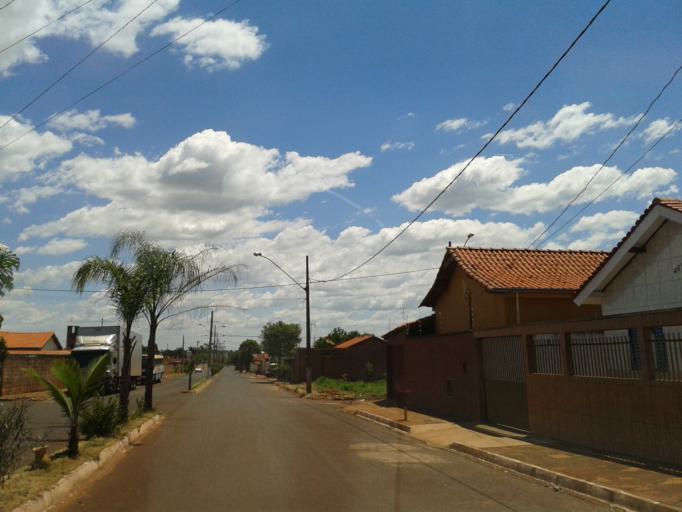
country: BR
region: Minas Gerais
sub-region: Centralina
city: Centralina
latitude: -18.7238
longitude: -49.1930
